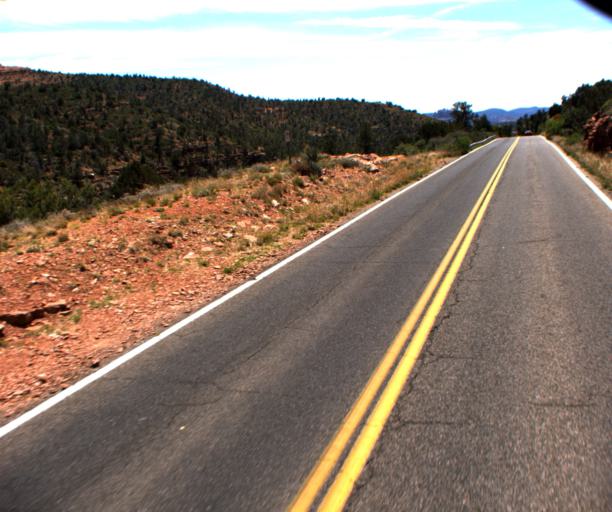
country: US
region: Arizona
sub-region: Coconino County
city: Sedona
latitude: 34.8835
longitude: -111.7459
